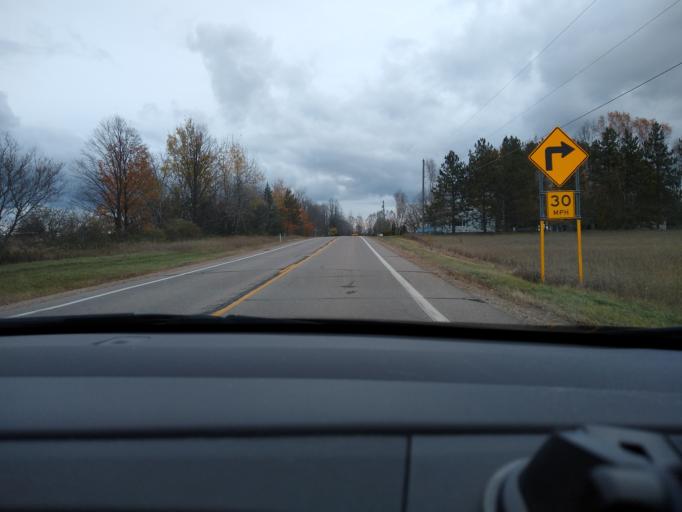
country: US
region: Michigan
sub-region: Delta County
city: Escanaba
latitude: 45.7389
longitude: -87.2661
